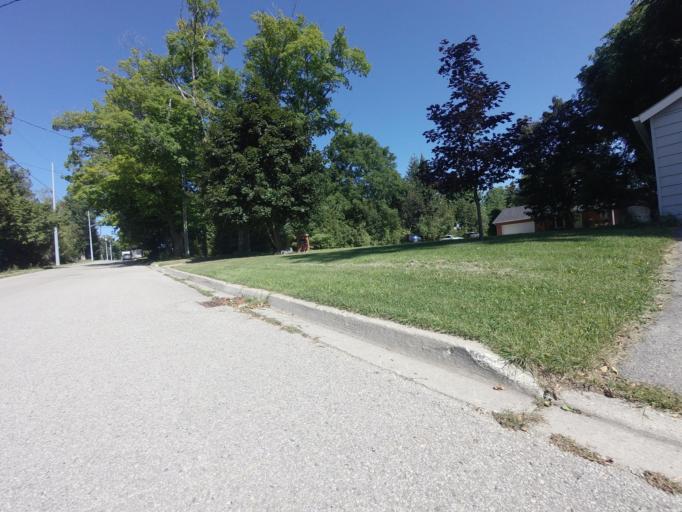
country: CA
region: Ontario
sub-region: Wellington County
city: Guelph
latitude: 43.6842
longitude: -80.4372
